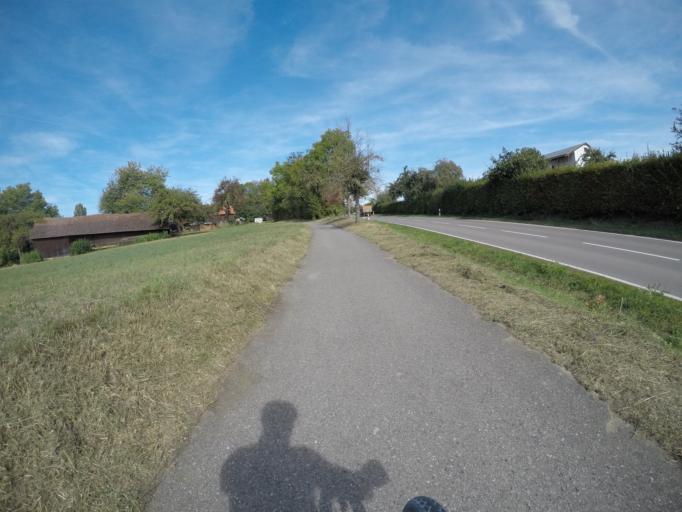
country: DE
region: Baden-Wuerttemberg
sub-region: Regierungsbezirk Stuttgart
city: Oberriexingen
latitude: 48.9349
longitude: 9.0229
